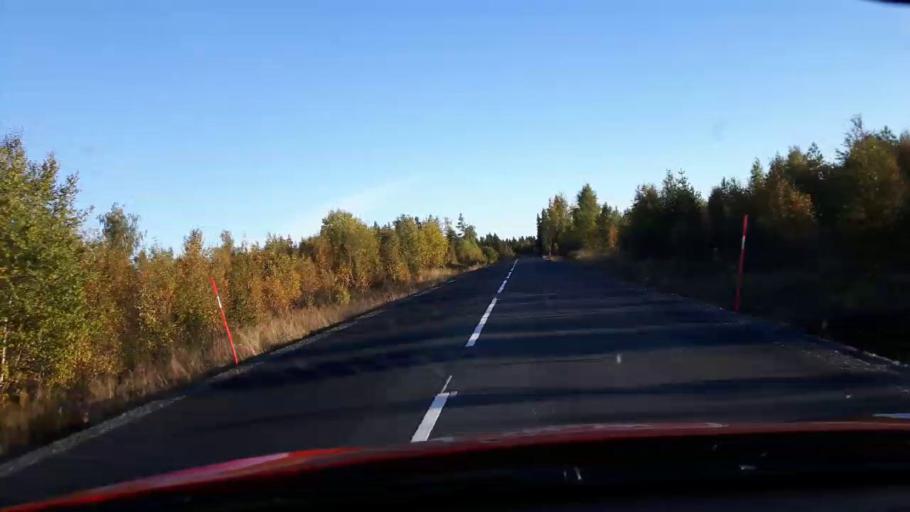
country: SE
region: Jaemtland
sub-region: OEstersunds Kommun
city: Lit
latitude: 63.4933
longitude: 14.8762
